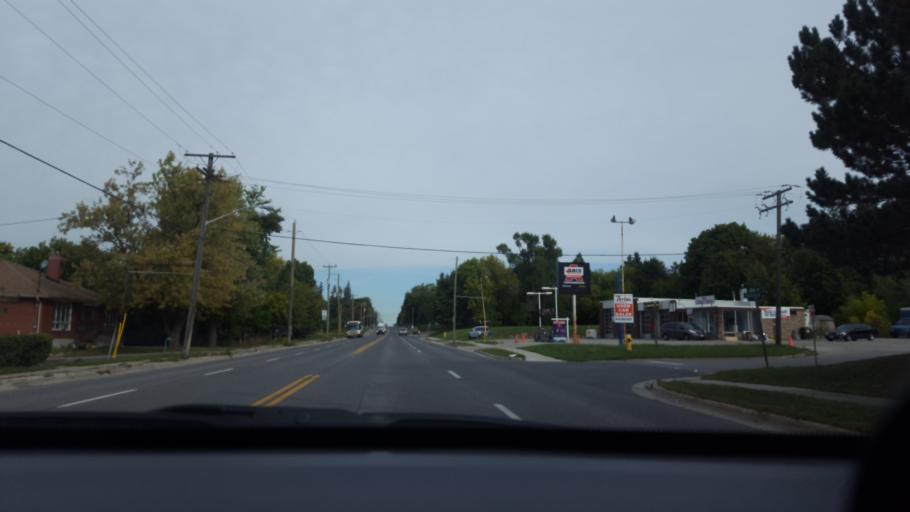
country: CA
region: Ontario
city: Vaughan
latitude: 43.9220
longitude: -79.5264
